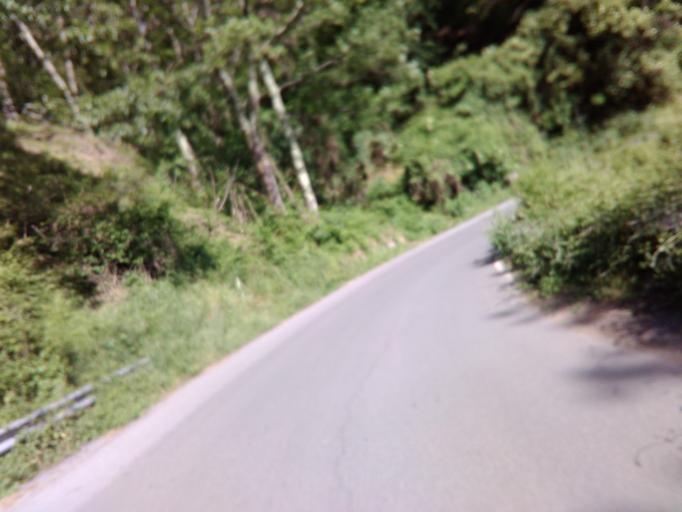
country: IT
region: Tuscany
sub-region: Provincia di Massa-Carrara
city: Fosdinovo
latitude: 44.1207
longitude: 10.0656
